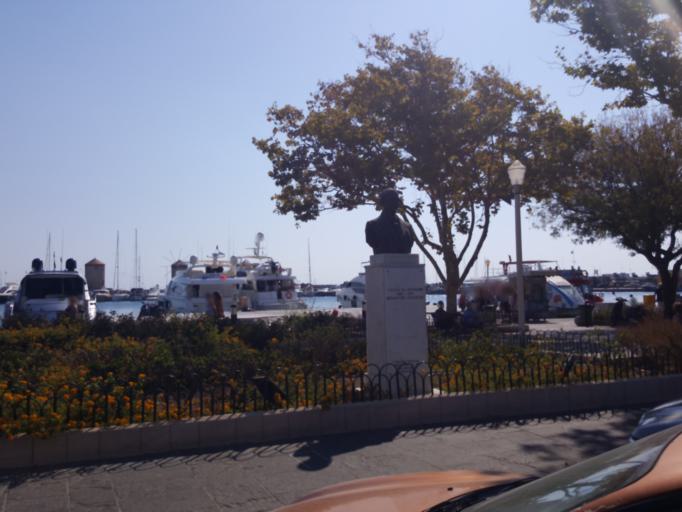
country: GR
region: South Aegean
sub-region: Nomos Dodekanisou
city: Rodos
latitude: 36.4489
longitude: 28.2253
